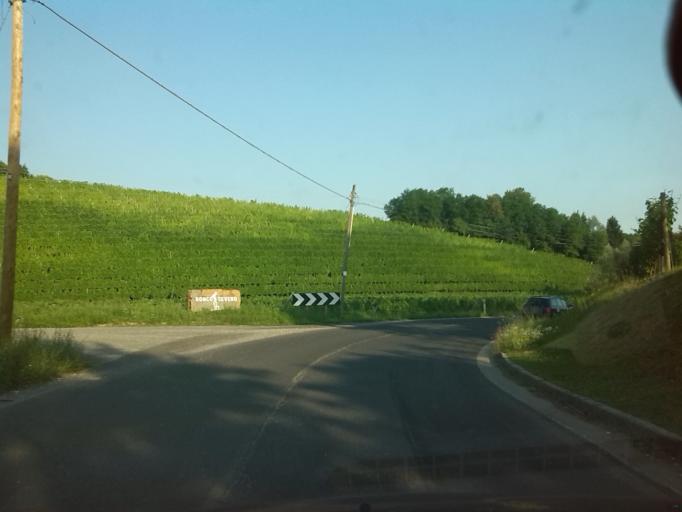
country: IT
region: Friuli Venezia Giulia
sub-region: Provincia di Udine
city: Prepotto
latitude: 46.0536
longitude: 13.4617
